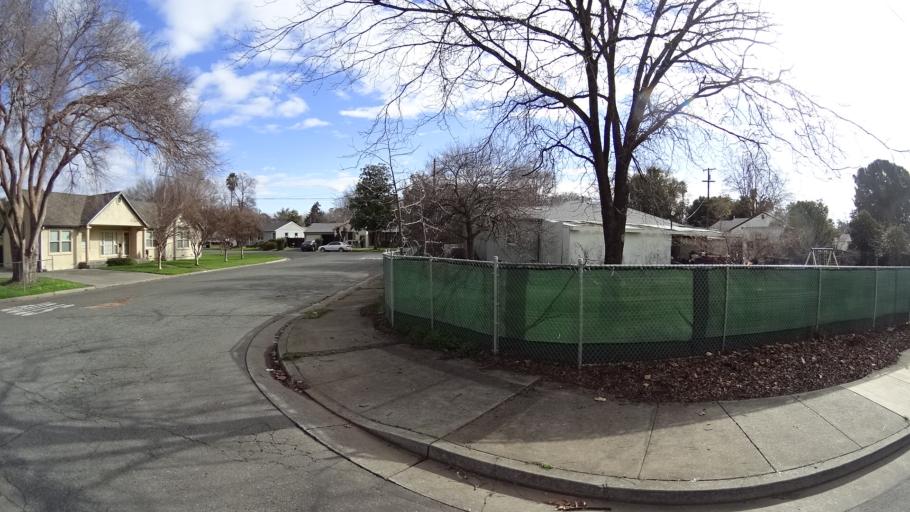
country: US
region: California
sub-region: Butte County
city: Oroville
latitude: 39.5245
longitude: -121.5586
